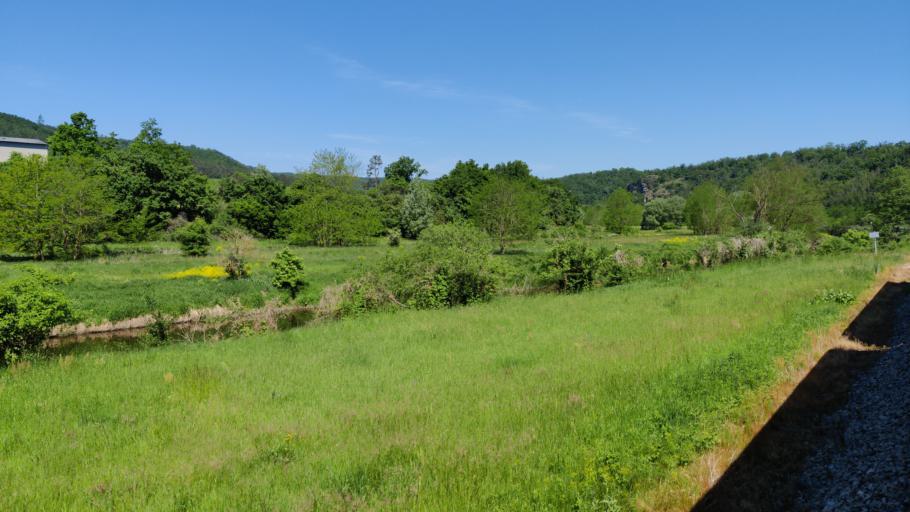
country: AT
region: Lower Austria
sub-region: Politischer Bezirk Horn
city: Gars am Kamp
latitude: 48.5645
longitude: 15.6728
